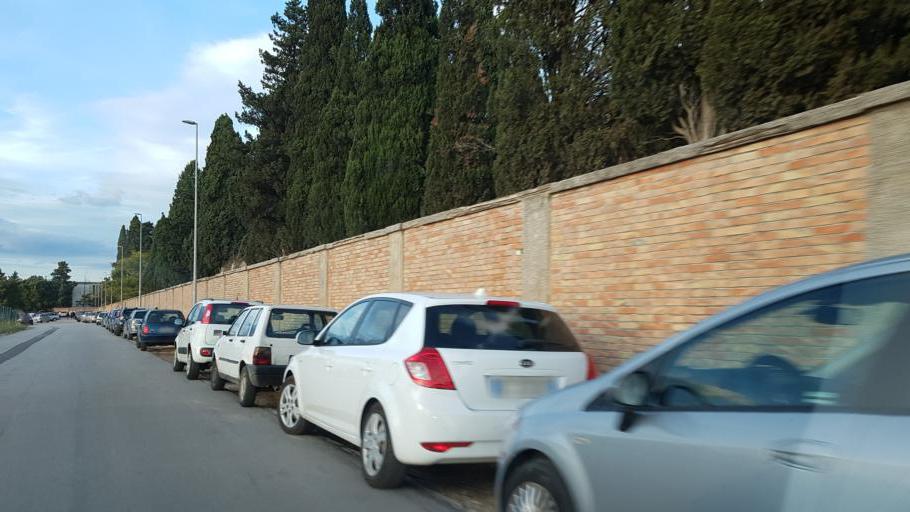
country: IT
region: Apulia
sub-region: Provincia di Foggia
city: Foggia
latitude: 41.4745
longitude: 15.5473
